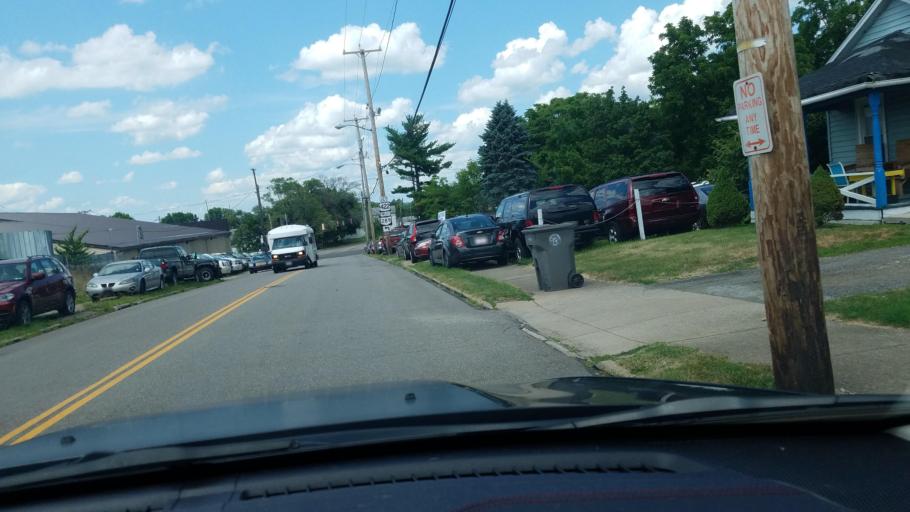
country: US
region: Ohio
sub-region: Mahoning County
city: Youngstown
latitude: 41.0994
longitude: -80.6320
